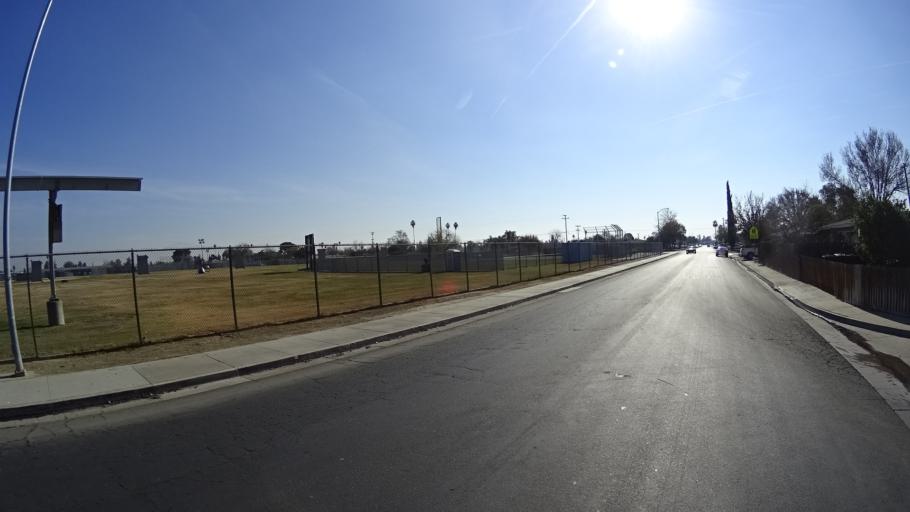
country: US
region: California
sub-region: Kern County
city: Bakersfield
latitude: 35.3223
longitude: -119.0163
